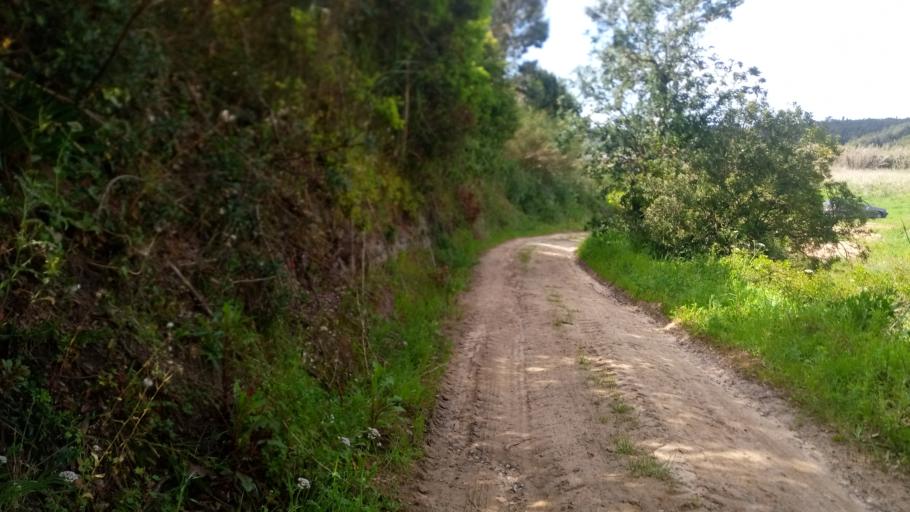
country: PT
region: Leiria
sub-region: Caldas da Rainha
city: Caldas da Rainha
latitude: 39.3996
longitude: -9.1826
